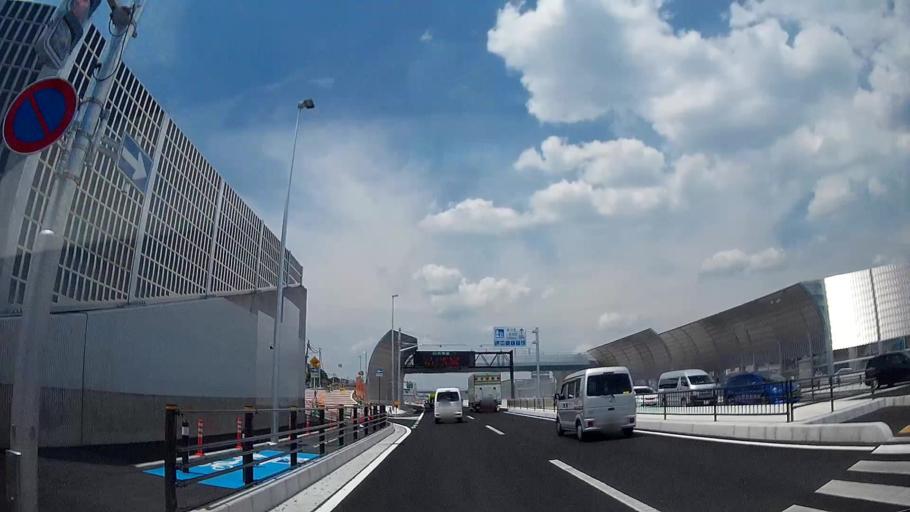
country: JP
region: Chiba
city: Matsudo
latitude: 35.7438
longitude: 139.9197
